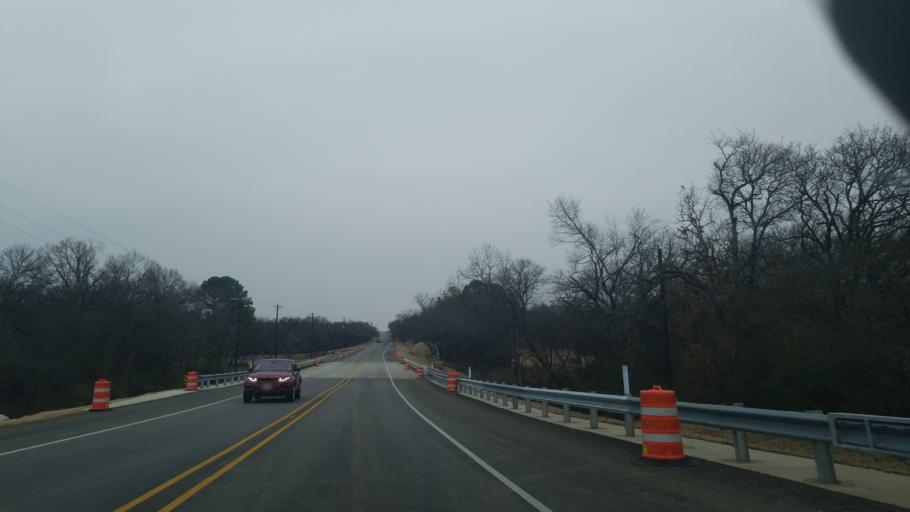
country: US
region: Texas
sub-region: Denton County
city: Argyle
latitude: 33.1257
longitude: -97.1395
